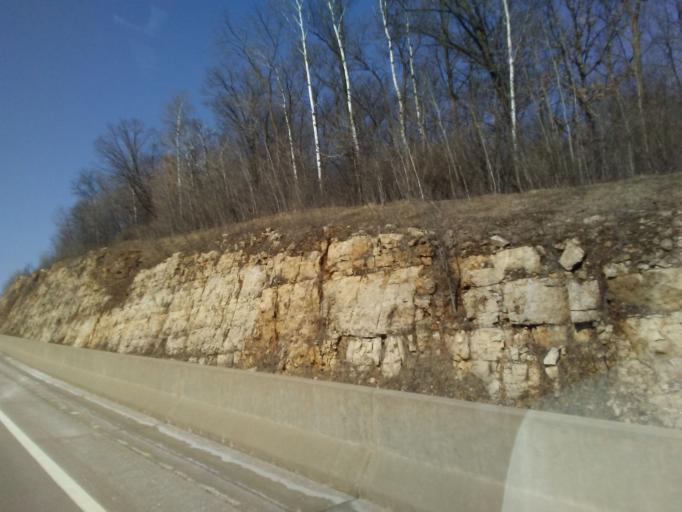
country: US
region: Wisconsin
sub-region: La Crosse County
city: West Salem
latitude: 43.7104
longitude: -91.0621
